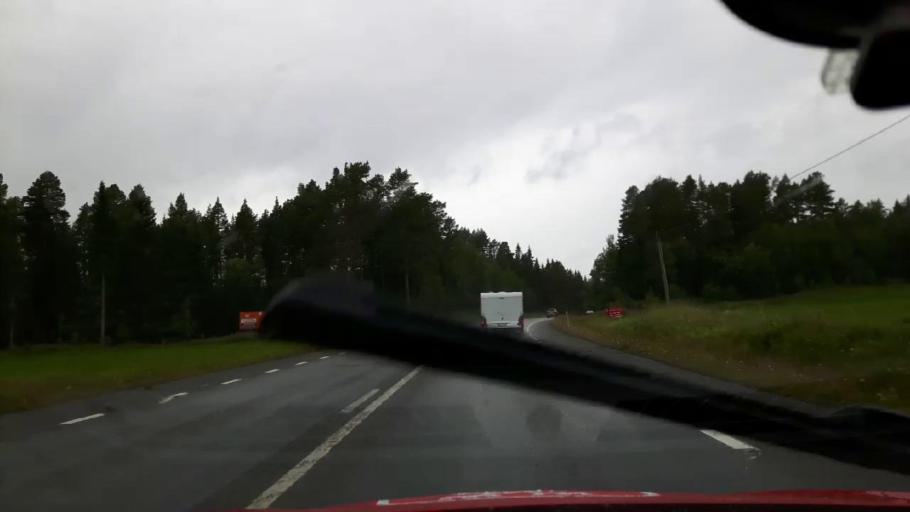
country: SE
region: Jaemtland
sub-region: Are Kommun
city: Jarpen
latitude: 63.3365
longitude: 13.5062
